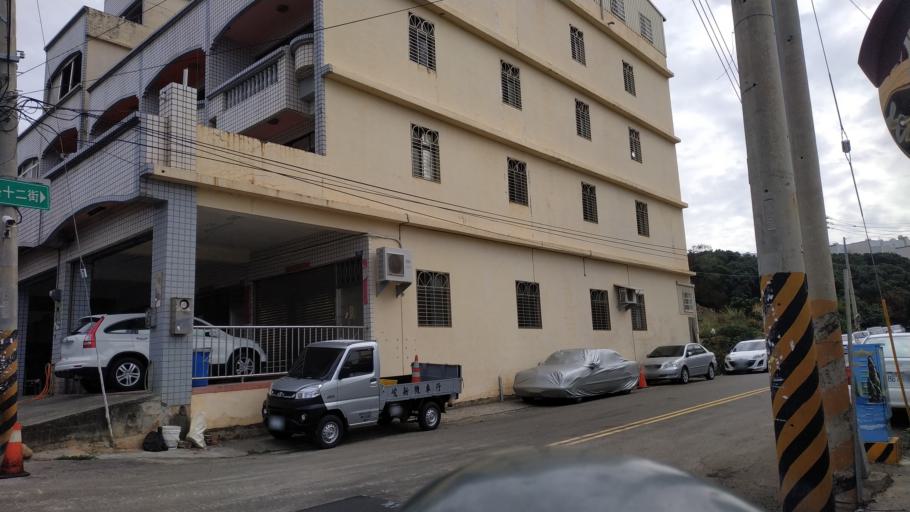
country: TW
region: Taiwan
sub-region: Taichung City
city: Taichung
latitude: 24.2146
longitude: 120.5765
